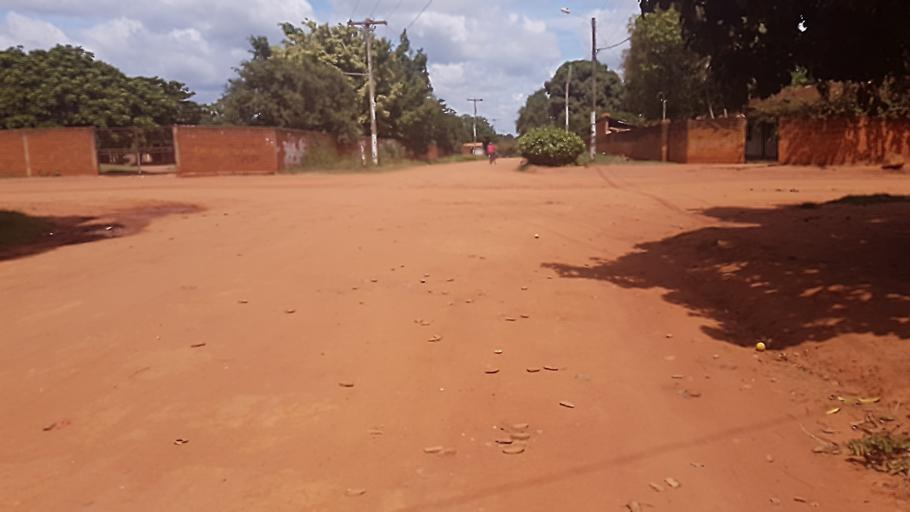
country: BO
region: Santa Cruz
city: San Ignacio de Velasco
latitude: -16.3744
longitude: -60.9657
